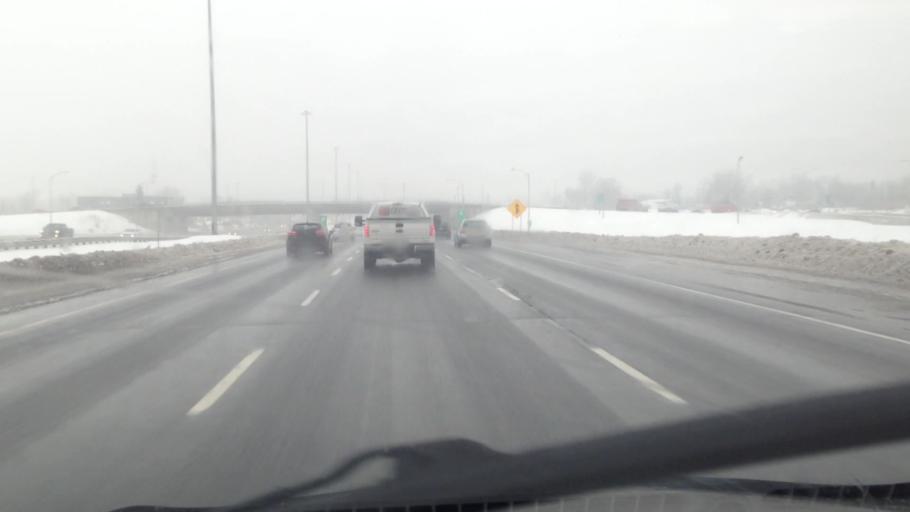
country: CA
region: Quebec
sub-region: Laurentides
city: Boisbriand
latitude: 45.5976
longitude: -73.8037
